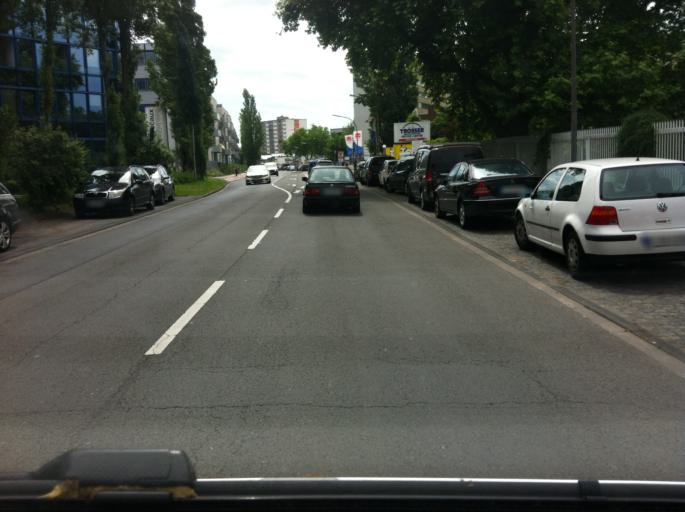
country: DE
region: North Rhine-Westphalia
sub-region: Regierungsbezirk Koln
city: Neuehrenfeld
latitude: 50.9444
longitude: 6.9077
